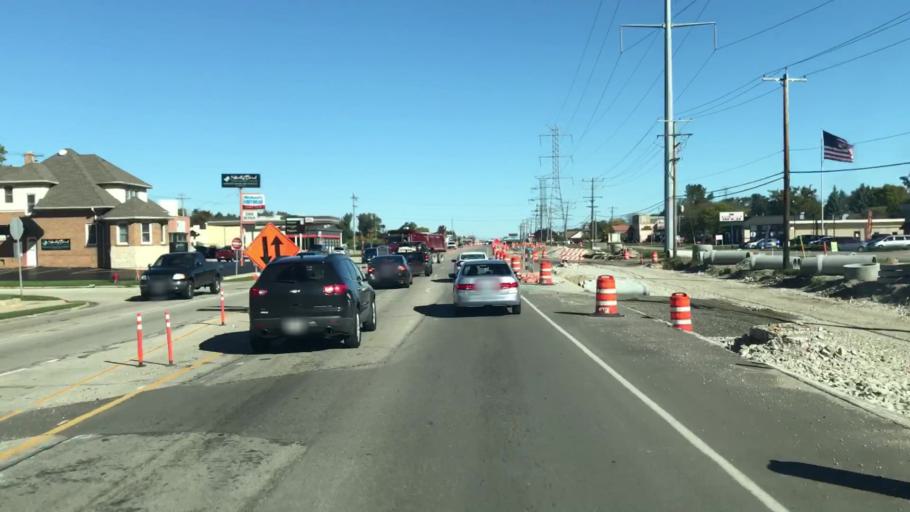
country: US
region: Wisconsin
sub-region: Milwaukee County
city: Hales Corners
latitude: 42.9452
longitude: -88.0483
